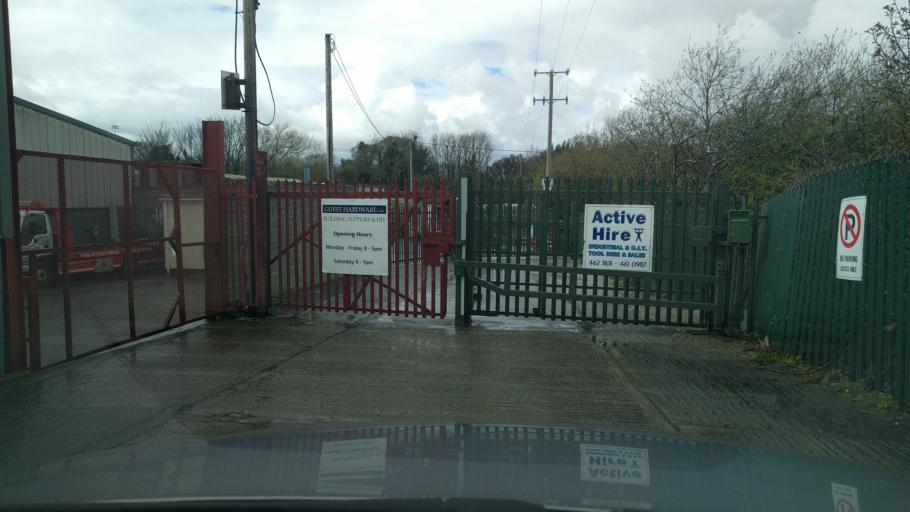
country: IE
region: Leinster
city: Oldbawn
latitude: 53.2703
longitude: -6.3587
